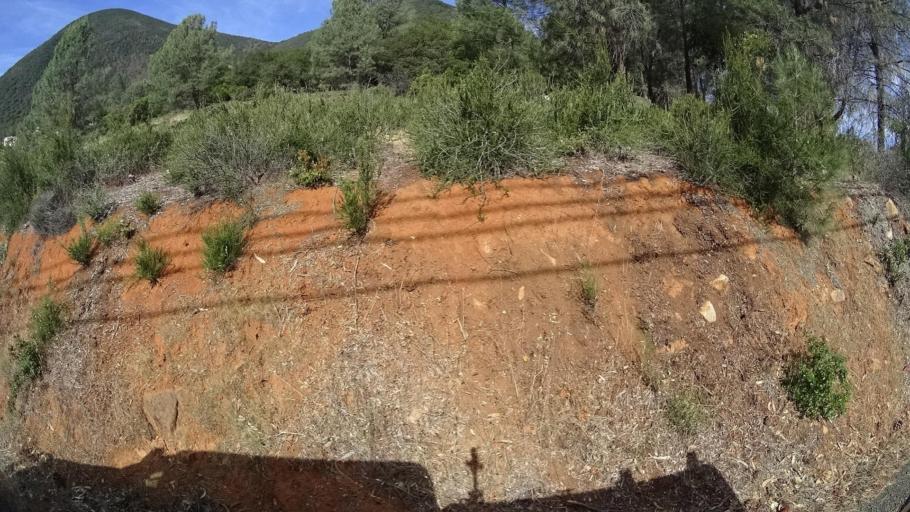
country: US
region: California
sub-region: Lake County
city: Soda Bay
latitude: 38.9906
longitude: -122.7440
